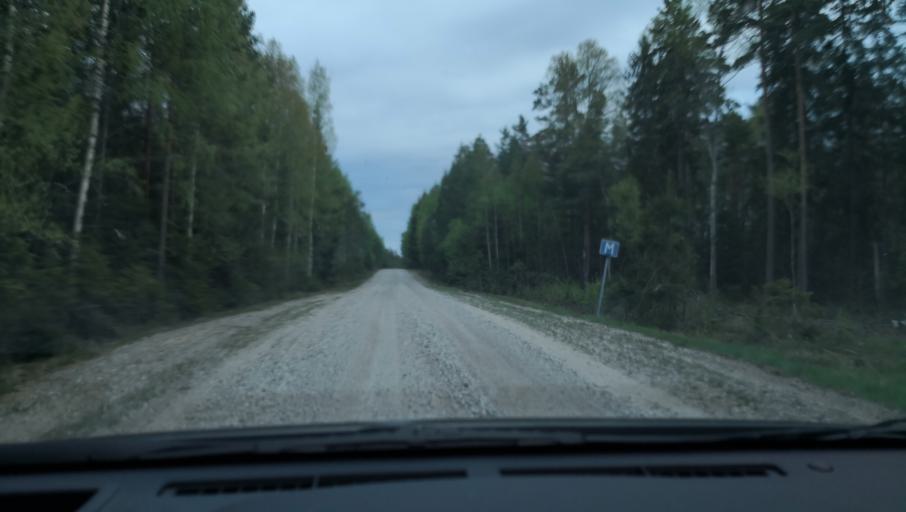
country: SE
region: Vaestmanland
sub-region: Skinnskattebergs Kommun
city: Skinnskatteberg
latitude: 59.7670
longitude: 15.4566
